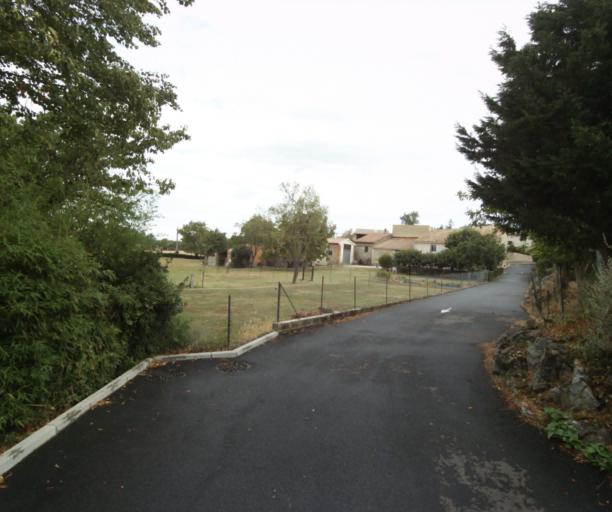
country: FR
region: Midi-Pyrenees
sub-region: Departement de la Haute-Garonne
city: Revel
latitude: 43.4355
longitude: 1.9663
